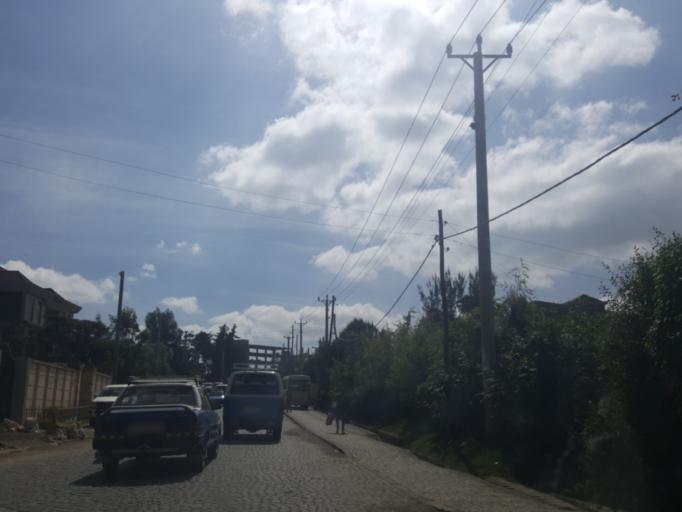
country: ET
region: Adis Abeba
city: Addis Ababa
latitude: 9.0515
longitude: 38.7266
